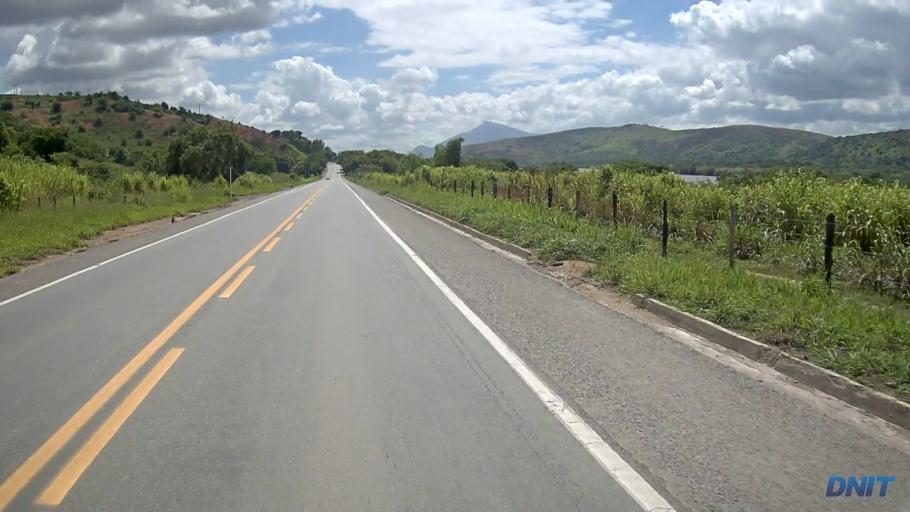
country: BR
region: Minas Gerais
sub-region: Governador Valadares
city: Governador Valadares
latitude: -18.9657
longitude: -42.0817
